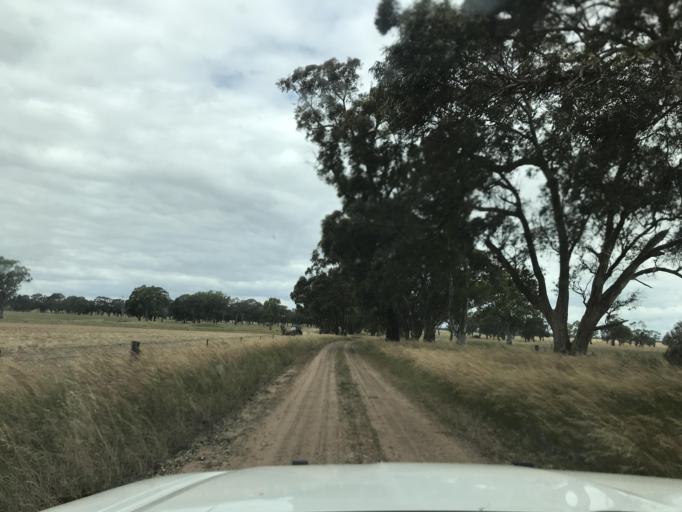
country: AU
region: South Australia
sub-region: Naracoorte and Lucindale
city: Naracoorte
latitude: -36.9247
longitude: 141.3060
